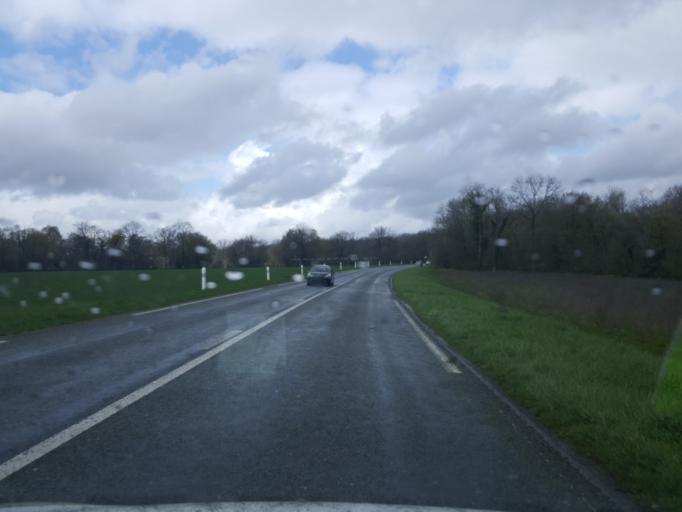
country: FR
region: Haute-Normandie
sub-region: Departement de l'Eure
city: Gisors
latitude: 49.2422
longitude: 1.7985
